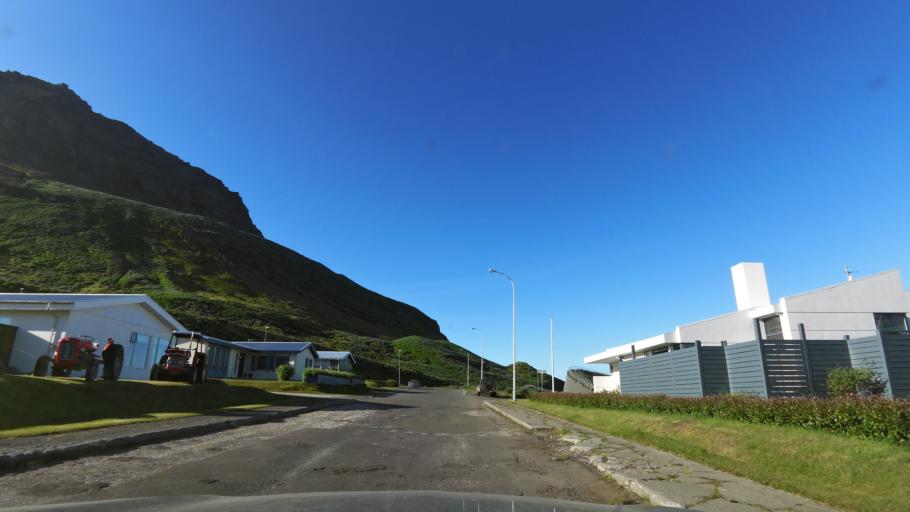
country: IS
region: Westfjords
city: Isafjoerdur
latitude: 66.1606
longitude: -23.2568
